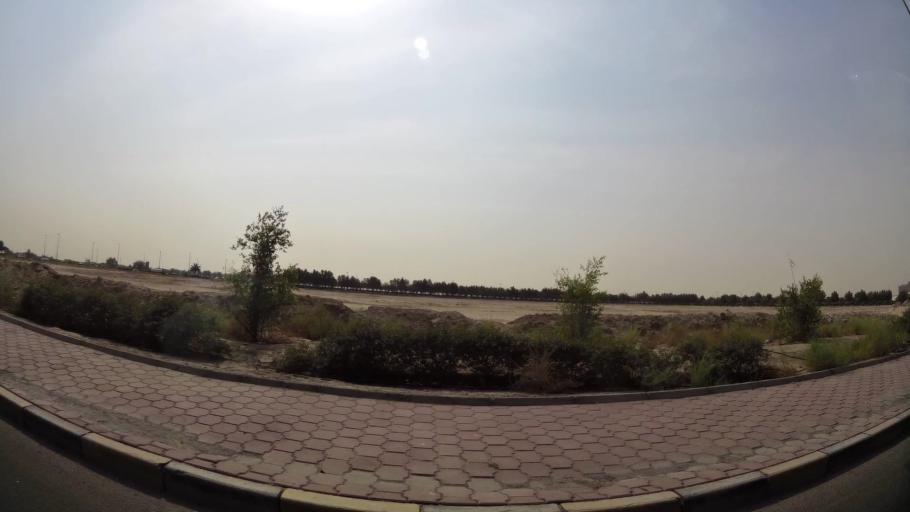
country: KW
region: Al Farwaniyah
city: Al Farwaniyah
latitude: 29.2597
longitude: 47.9560
